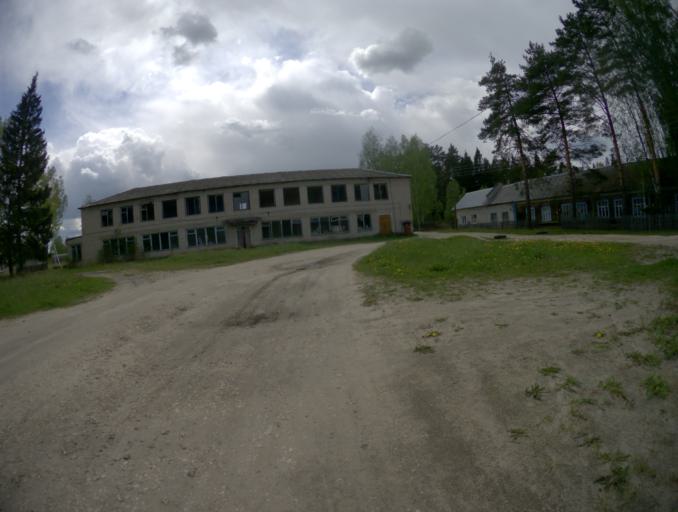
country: RU
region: Vladimir
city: Velikodvorskiy
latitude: 55.2385
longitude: 40.6526
